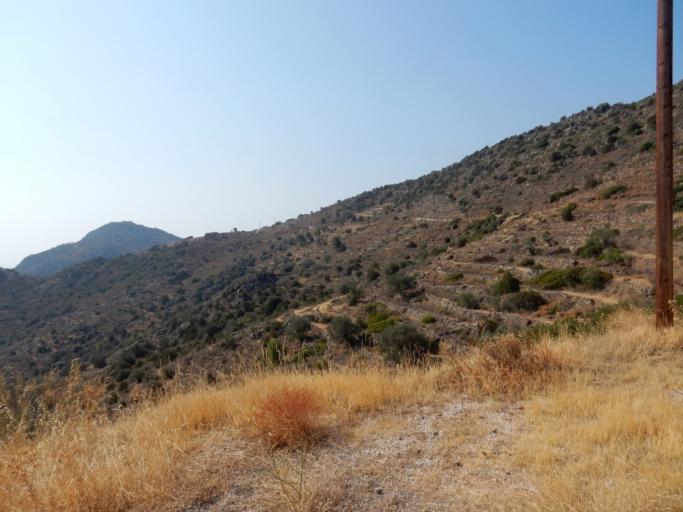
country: GR
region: Attica
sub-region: Nomos Piraios
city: Vathi
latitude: 37.7035
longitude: 23.5059
